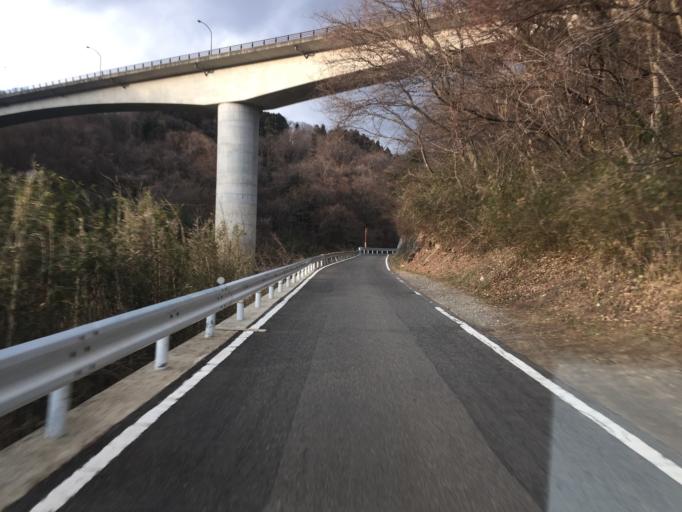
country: JP
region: Fukushima
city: Motomiya
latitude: 37.5346
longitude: 140.4162
